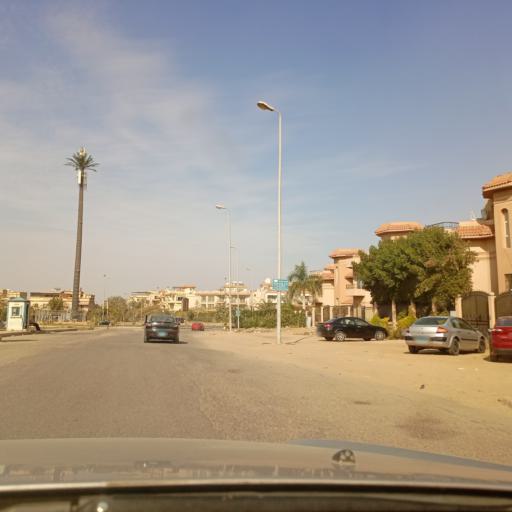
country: EG
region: Muhafazat al Qalyubiyah
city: Al Khankah
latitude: 30.0524
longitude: 31.4853
